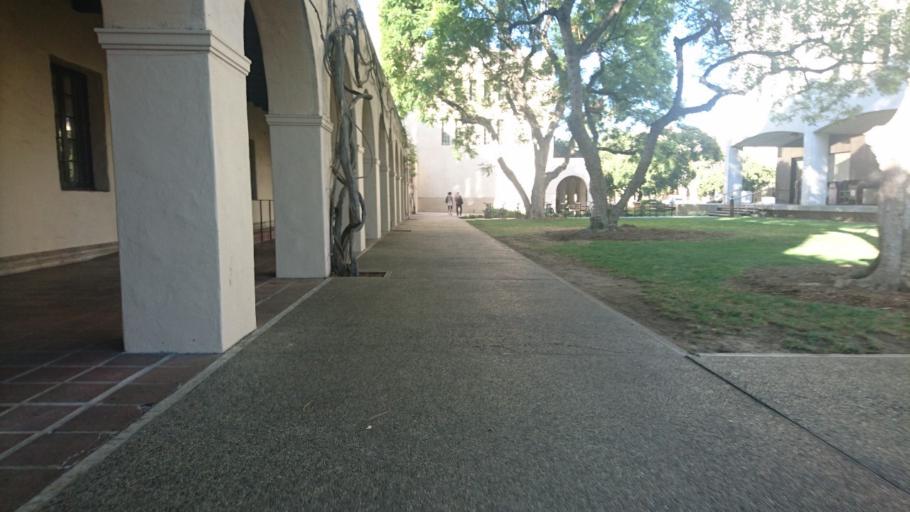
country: US
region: California
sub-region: Los Angeles County
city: Pasadena
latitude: 34.1366
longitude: -118.1258
